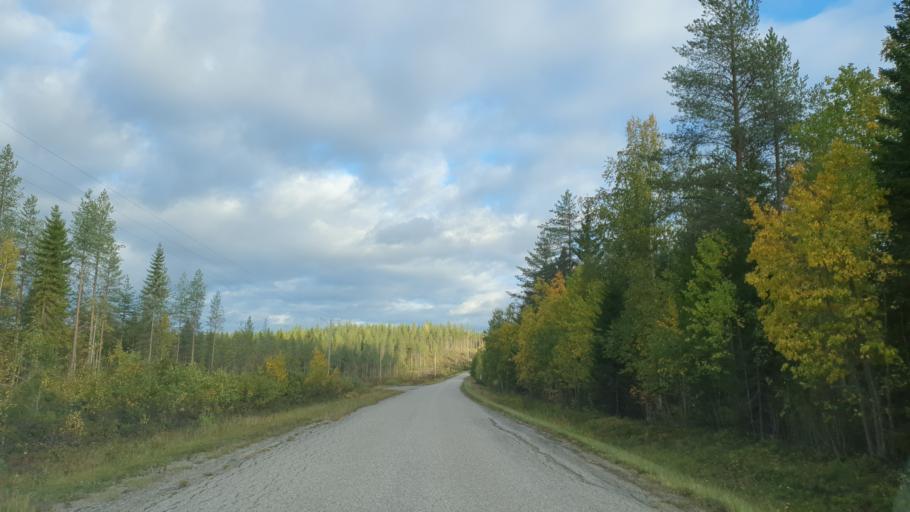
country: FI
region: Kainuu
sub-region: Kehys-Kainuu
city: Kuhmo
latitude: 63.9185
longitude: 30.0620
